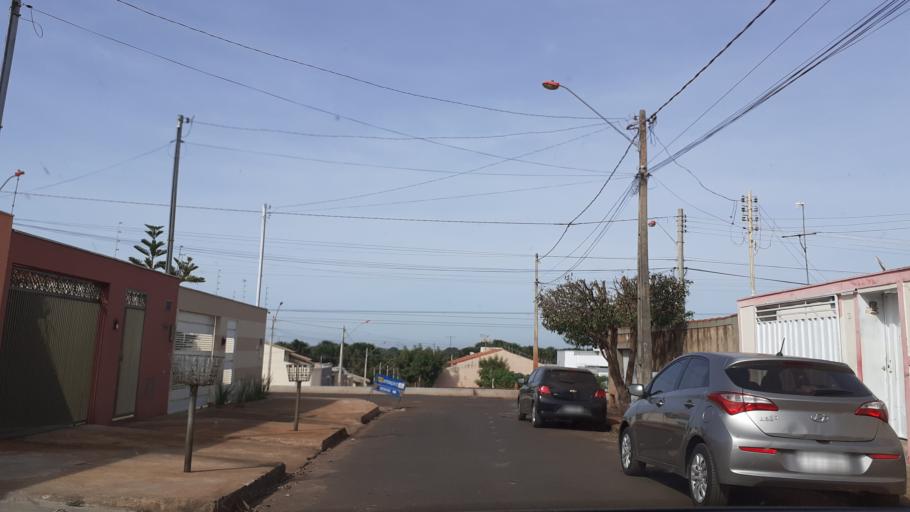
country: BR
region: Goias
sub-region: Itumbiara
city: Itumbiara
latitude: -18.4184
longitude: -49.2386
